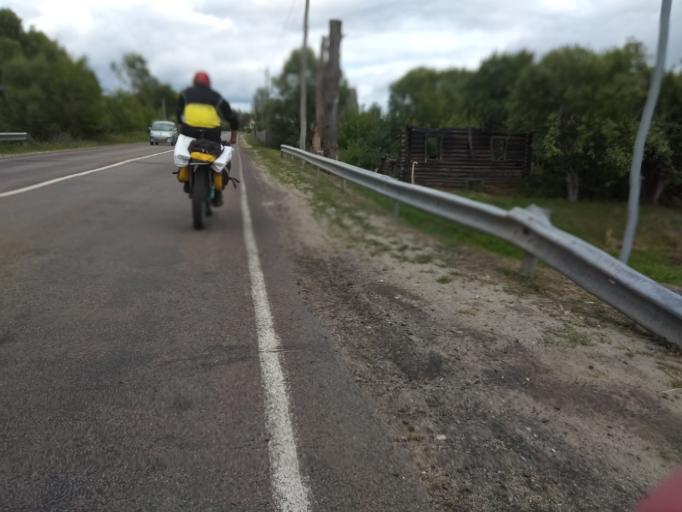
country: RU
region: Moskovskaya
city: Misheronskiy
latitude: 55.6008
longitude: 39.7060
